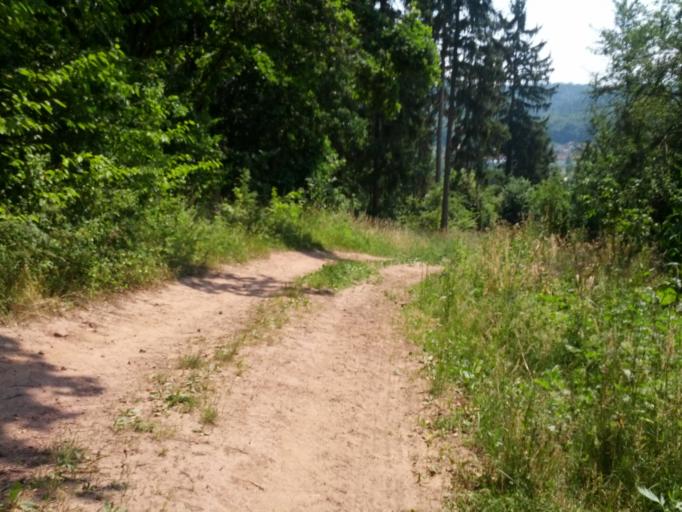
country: DE
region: Thuringia
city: Eisenach
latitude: 50.9851
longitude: 10.2879
